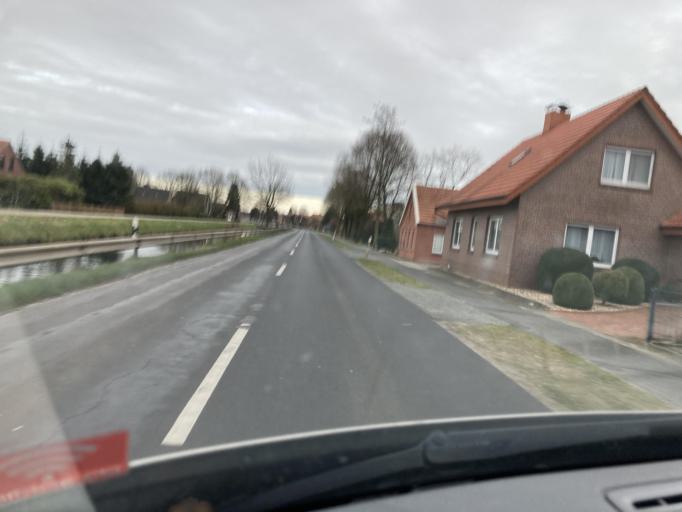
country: DE
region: Lower Saxony
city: Ostrhauderfehn
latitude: 53.1296
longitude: 7.5057
